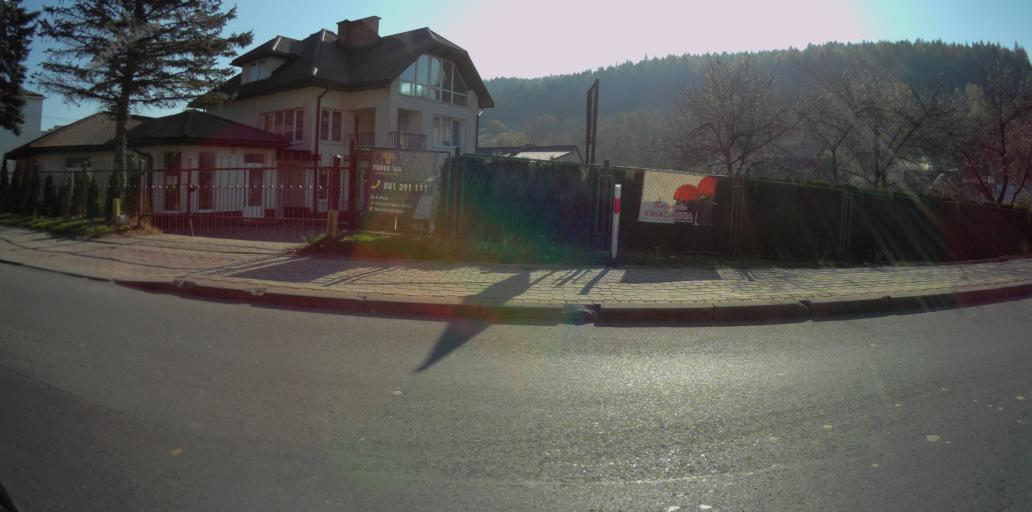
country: PL
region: Subcarpathian Voivodeship
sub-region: Powiat bieszczadzki
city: Ustrzyki Dolne
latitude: 49.4294
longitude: 22.5834
